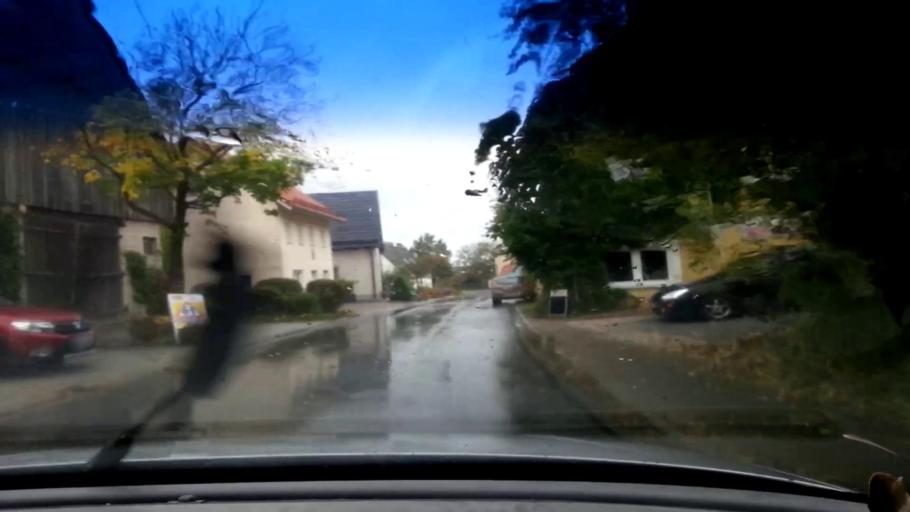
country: DE
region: Bavaria
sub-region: Upper Franconia
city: Stadelhofen
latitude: 50.0176
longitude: 11.1815
